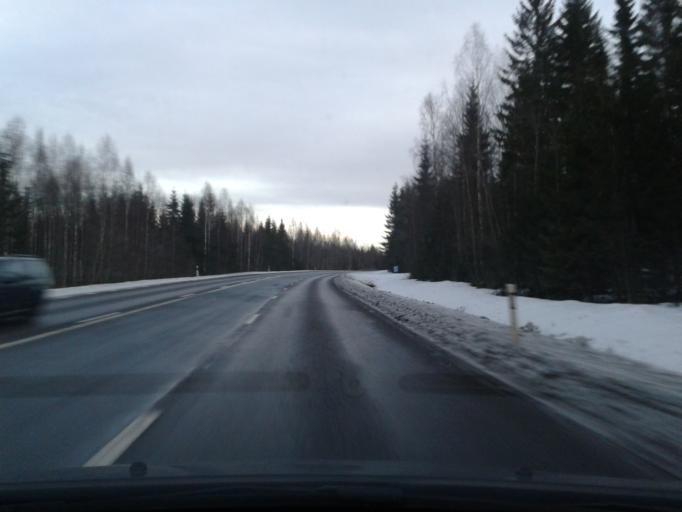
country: SE
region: Vaesternorrland
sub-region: Solleftea Kommun
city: Solleftea
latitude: 63.1404
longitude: 17.4292
